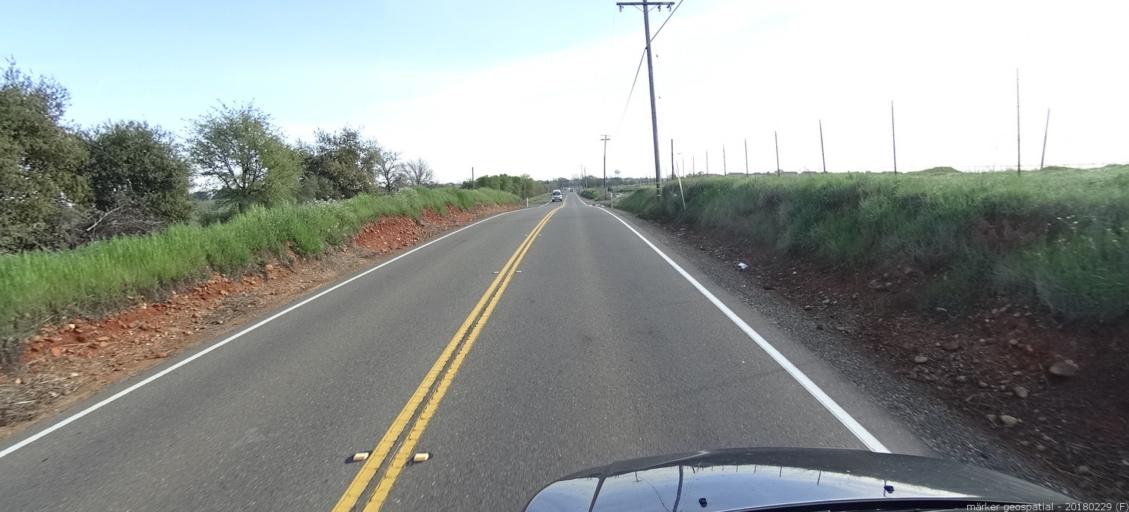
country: US
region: California
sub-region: Sacramento County
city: Rancho Cordova
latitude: 38.5352
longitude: -121.2933
